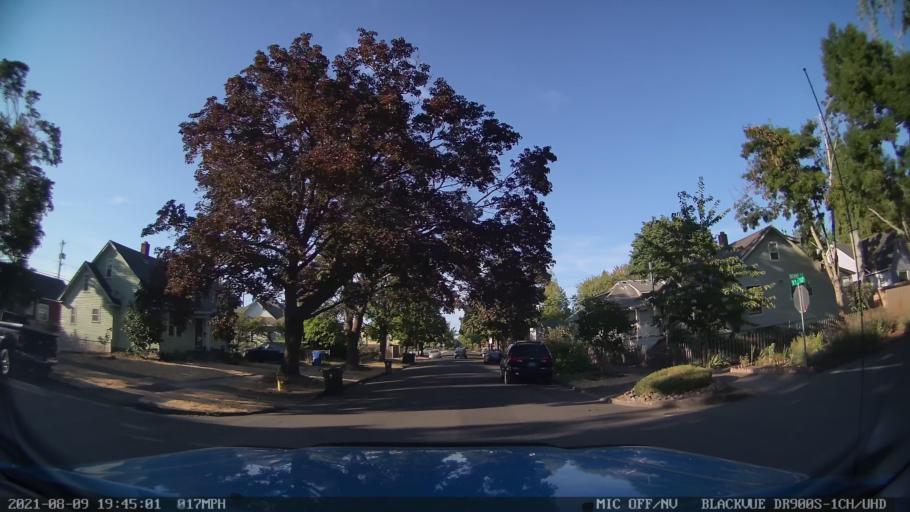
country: US
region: Oregon
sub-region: Marion County
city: Salem
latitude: 44.9498
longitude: -123.0306
